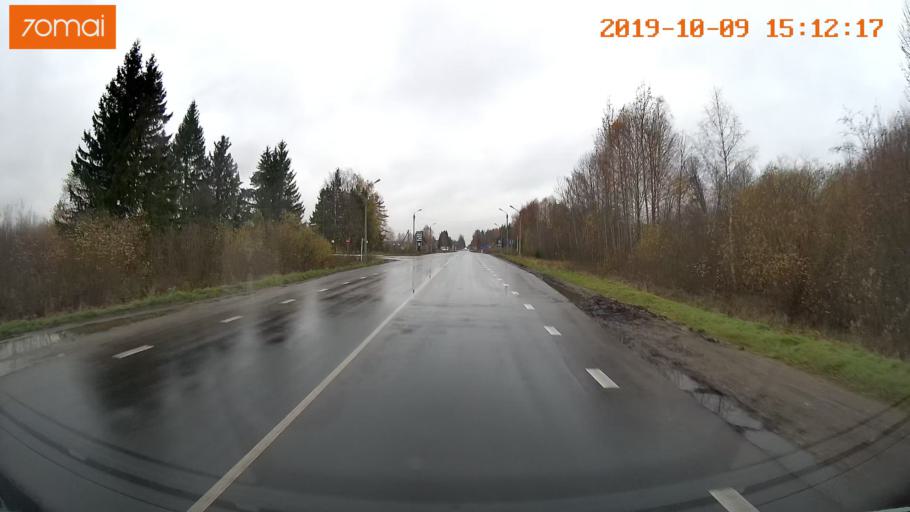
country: RU
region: Kostroma
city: Susanino
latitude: 58.1559
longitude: 41.6197
